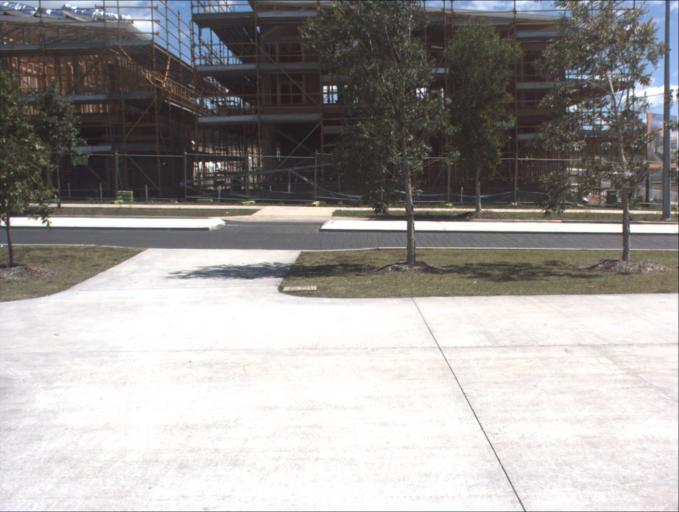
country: AU
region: Queensland
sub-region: Logan
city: Chambers Flat
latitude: -27.8036
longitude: 153.1033
